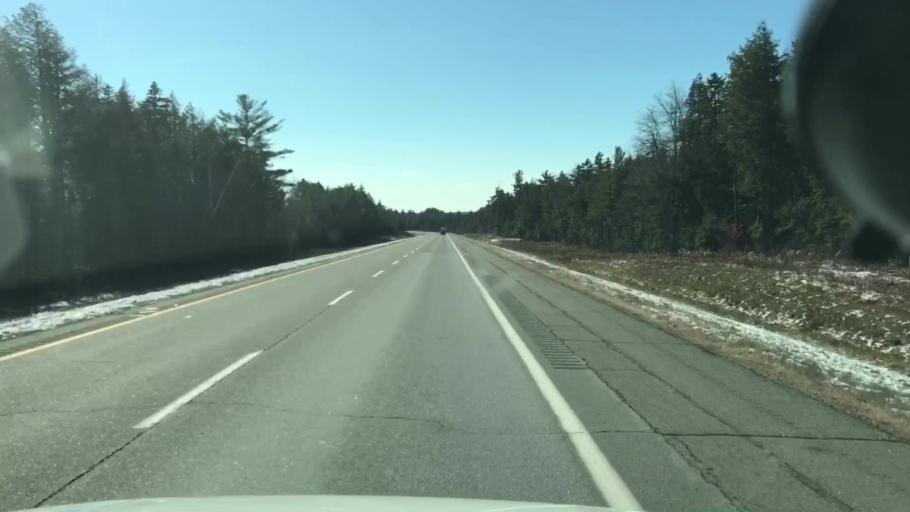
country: US
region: Maine
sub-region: Penobscot County
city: Howland
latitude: 45.2786
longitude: -68.6736
